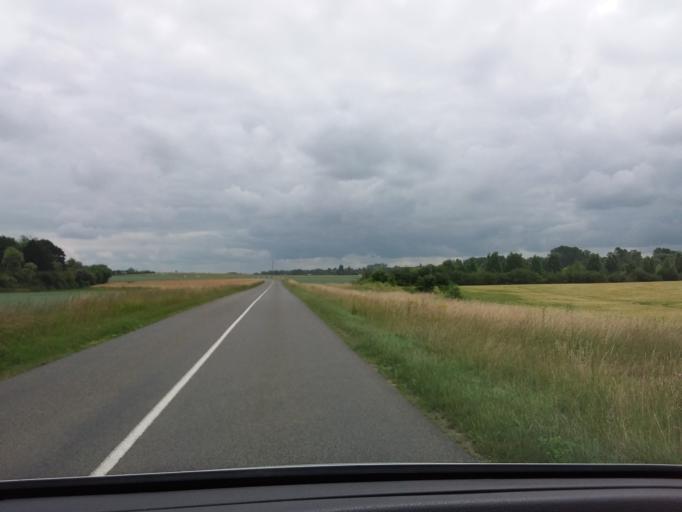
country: FR
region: Champagne-Ardenne
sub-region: Departement de la Marne
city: Cormicy
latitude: 49.4118
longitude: 3.8739
